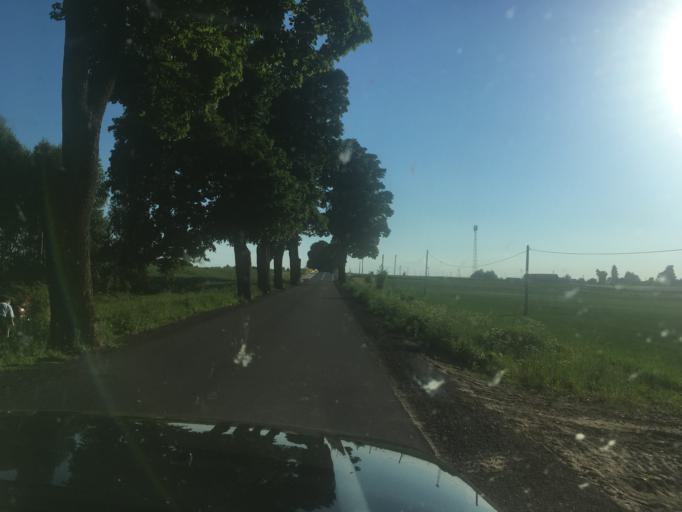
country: PL
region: Warmian-Masurian Voivodeship
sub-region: Powiat ostrodzki
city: Gierzwald
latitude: 53.6292
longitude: 20.0547
